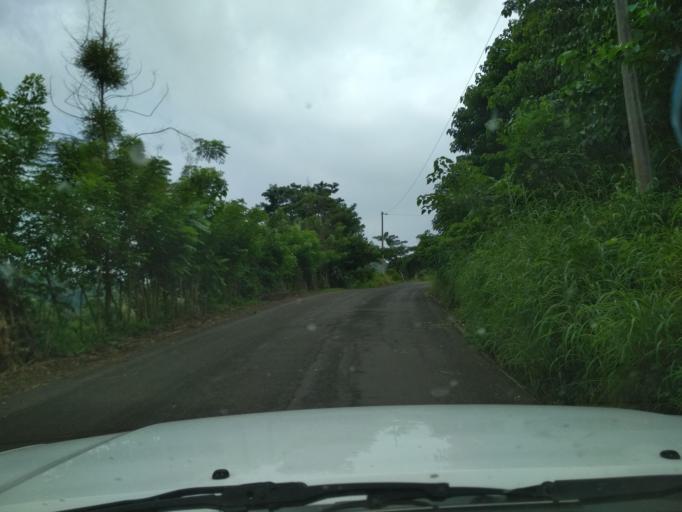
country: MX
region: Veracruz
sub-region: San Andres Tuxtla
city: El Huidero
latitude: 18.3840
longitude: -95.1778
